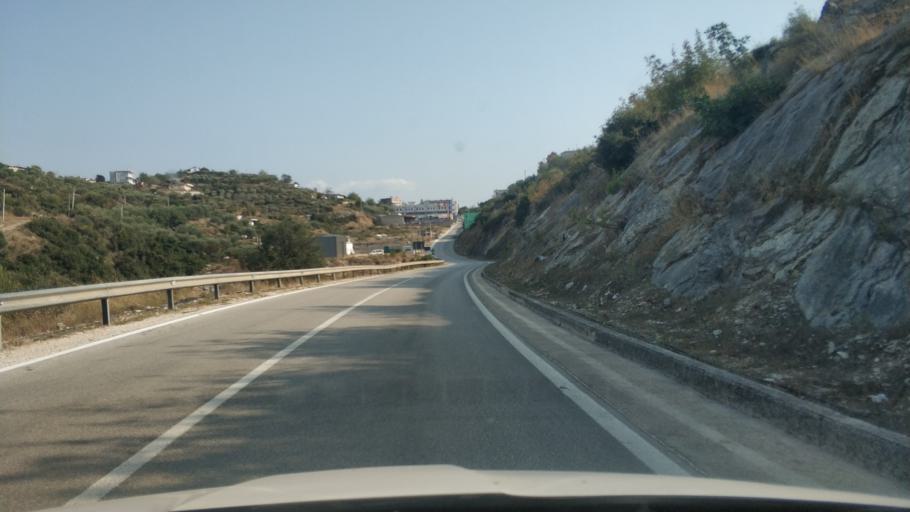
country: AL
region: Vlore
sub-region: Rrethi i Sarandes
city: Sarande
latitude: 39.8818
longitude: 20.0215
